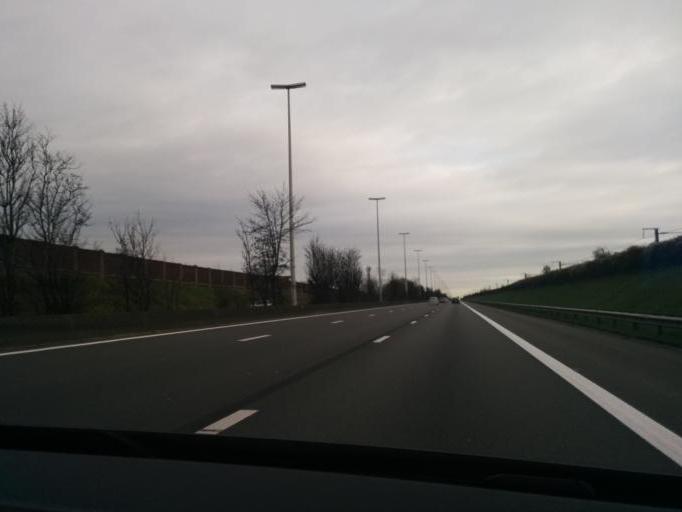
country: BE
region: Flanders
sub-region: Provincie Vlaams-Brabant
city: Bierbeek
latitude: 50.8339
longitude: 4.7809
